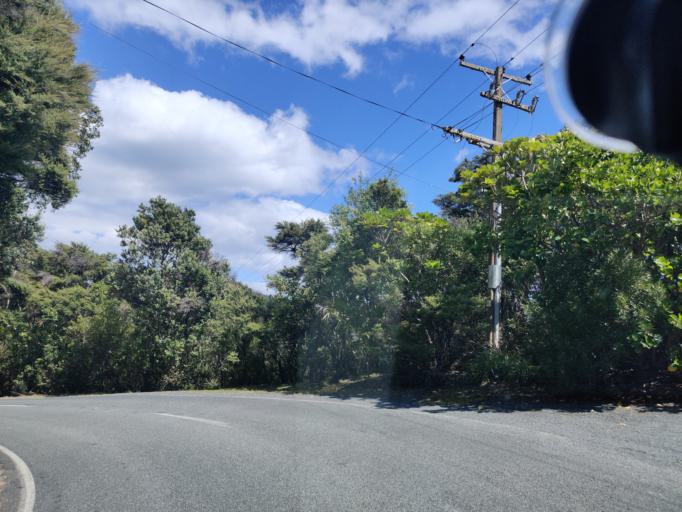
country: NZ
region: Northland
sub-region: Far North District
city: Paihia
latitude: -35.2568
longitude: 174.2391
